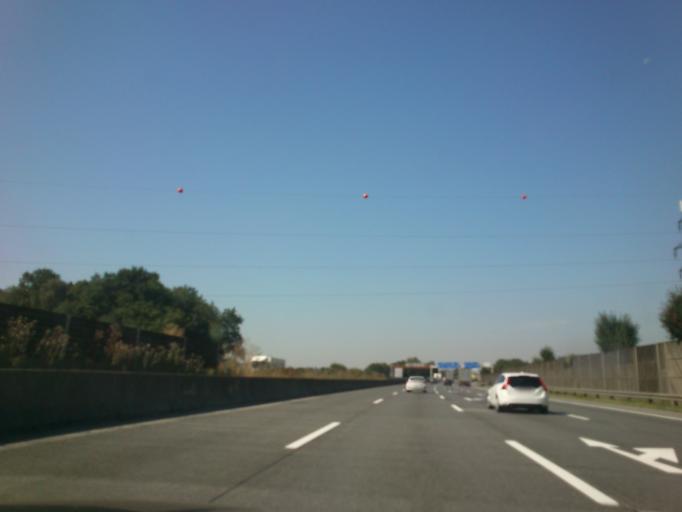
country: AT
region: Upper Austria
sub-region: Politischer Bezirk Linz-Land
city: Traun
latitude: 48.1948
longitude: 14.2412
